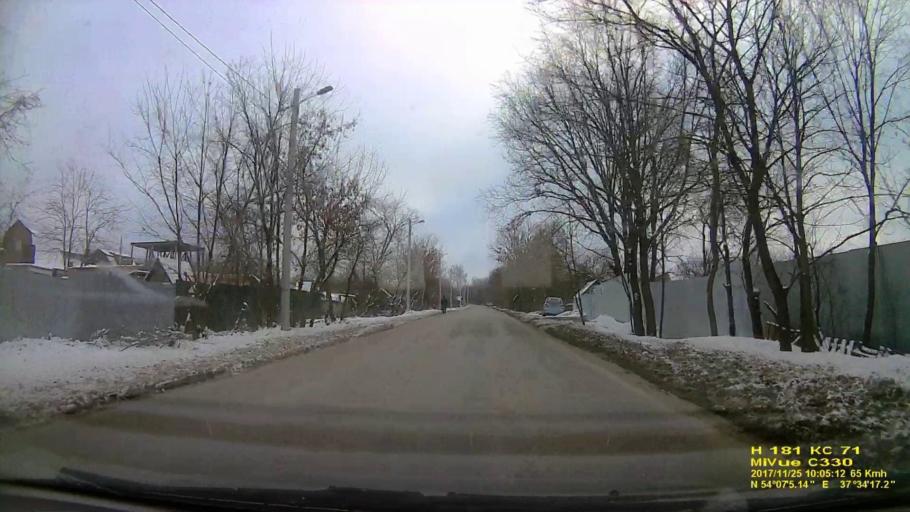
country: RU
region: Tula
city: Mendeleyevskiy
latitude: 54.1180
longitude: 37.5719
